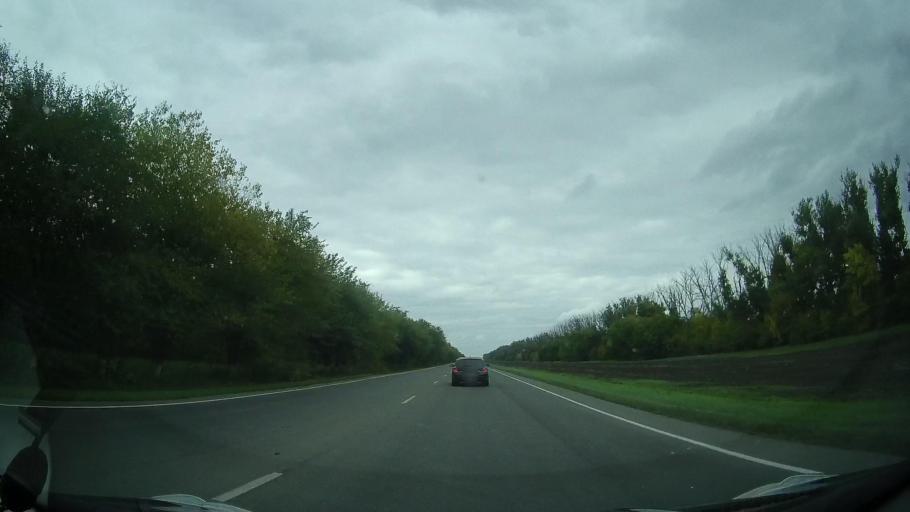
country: RU
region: Rostov
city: Yegorlykskaya
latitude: 46.6033
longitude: 40.6154
